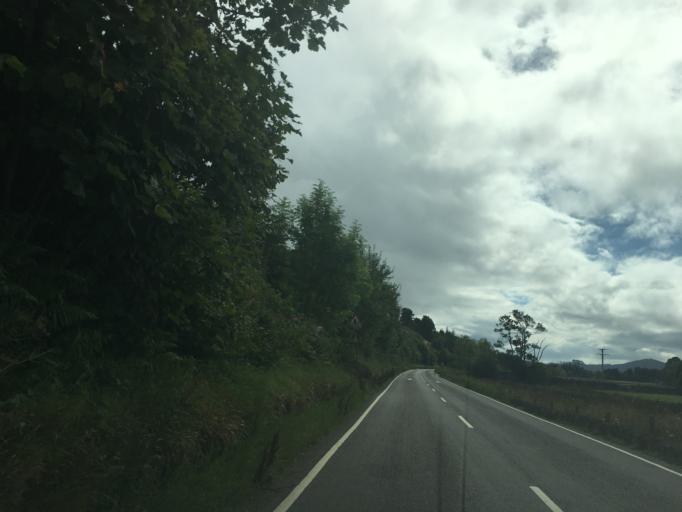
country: GB
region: Scotland
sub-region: Argyll and Bute
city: Lochgilphead
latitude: 56.1270
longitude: -5.4876
